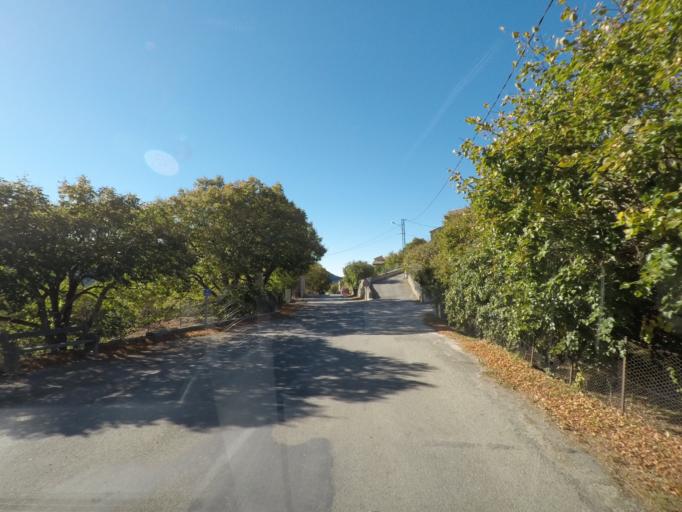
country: FR
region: Provence-Alpes-Cote d'Azur
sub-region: Departement des Hautes-Alpes
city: Serres
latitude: 44.4503
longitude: 5.5428
